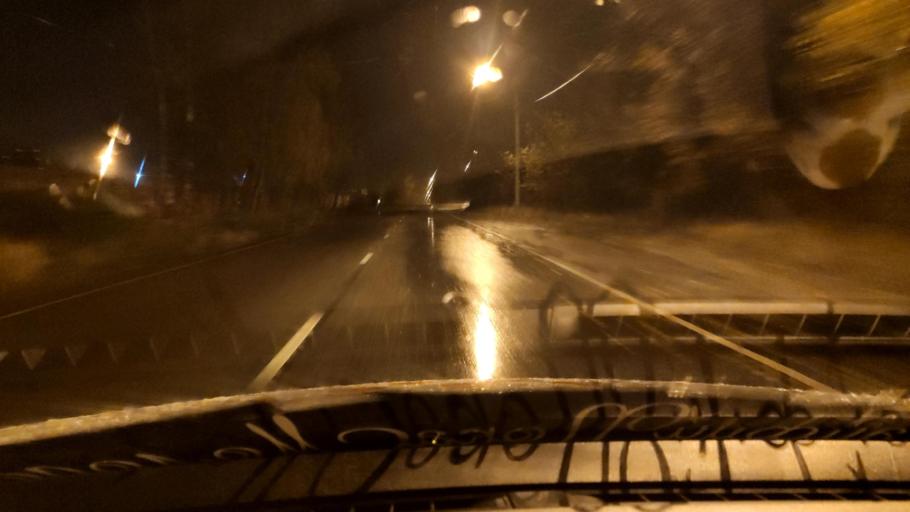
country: RU
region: Voronezj
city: Somovo
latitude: 51.7228
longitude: 39.2955
